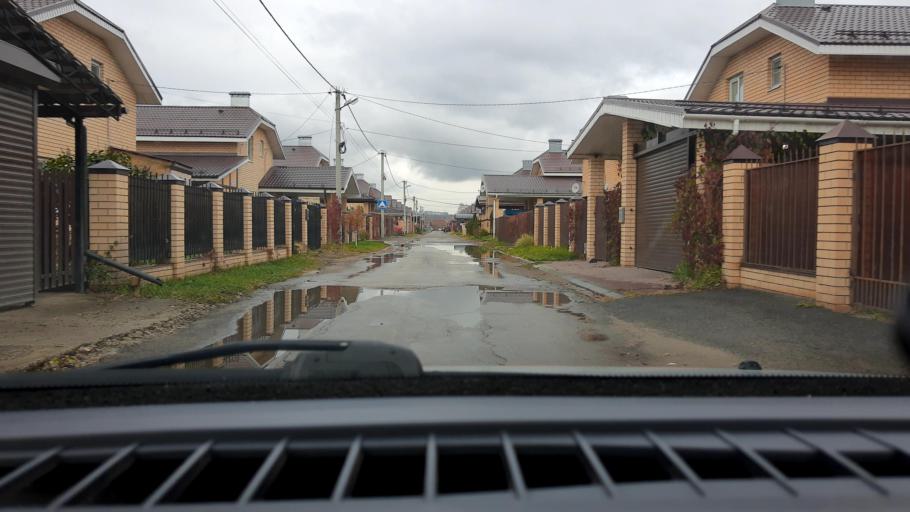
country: RU
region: Nizjnij Novgorod
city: Afonino
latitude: 56.2017
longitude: 44.1286
